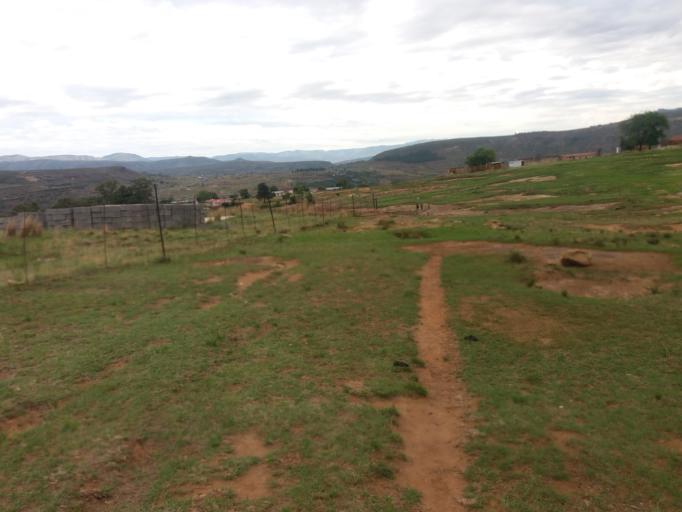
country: LS
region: Quthing
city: Quthing
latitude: -30.4084
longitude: 27.6977
